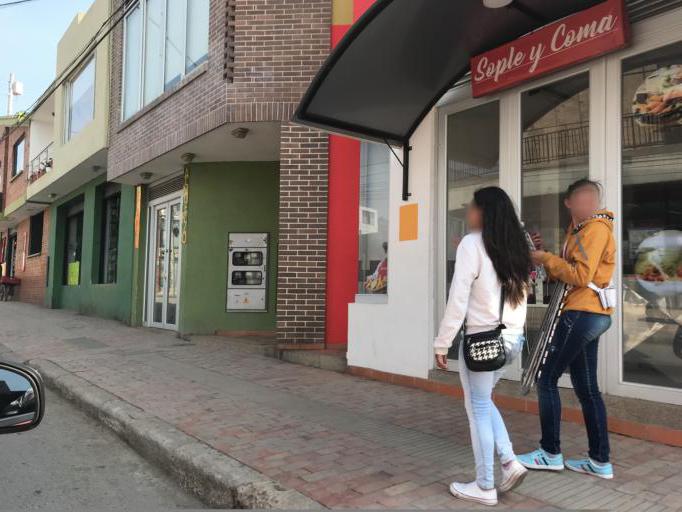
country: CO
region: Boyaca
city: Samaca
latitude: 5.4932
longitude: -73.4859
